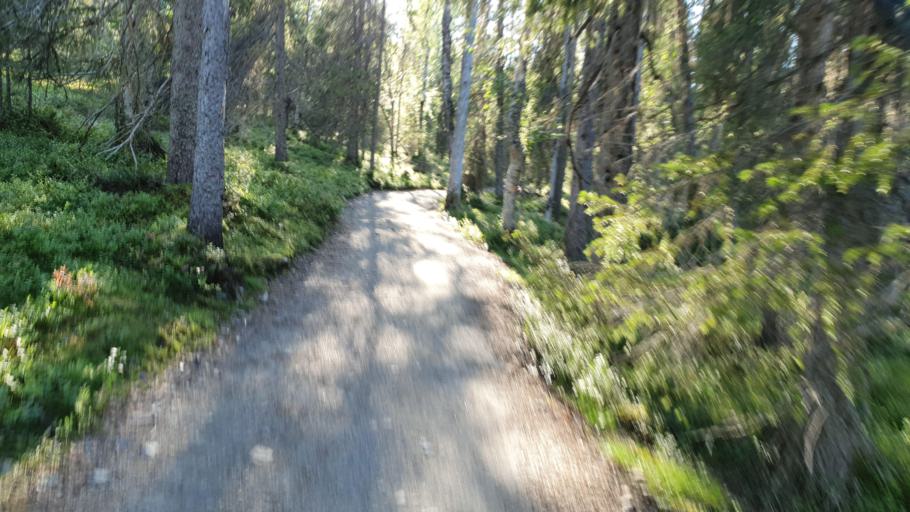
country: FI
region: Lapland
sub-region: Tunturi-Lappi
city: Kolari
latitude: 67.5983
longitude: 24.2117
